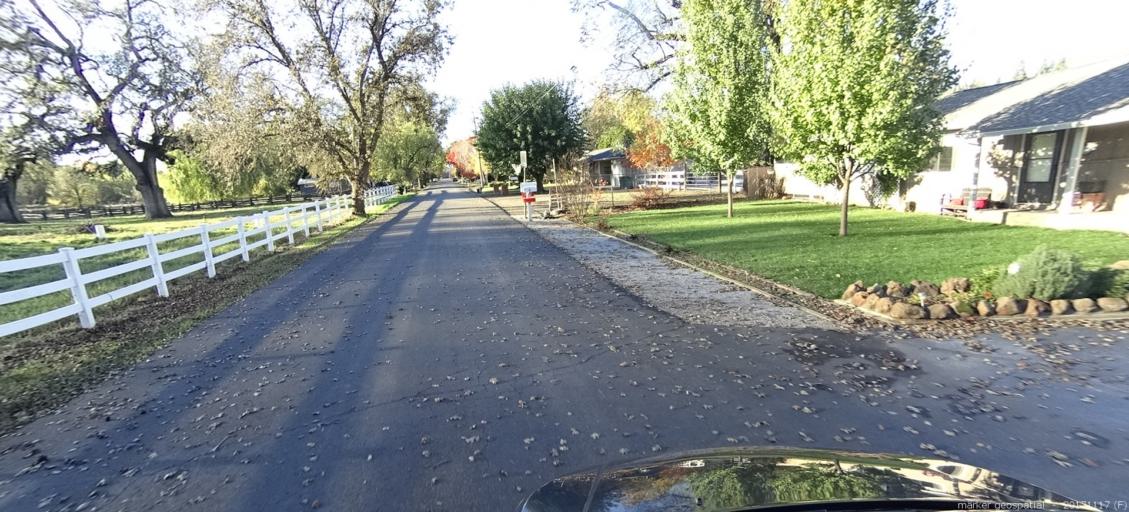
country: US
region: California
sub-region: Shasta County
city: Anderson
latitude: 40.4535
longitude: -122.2386
